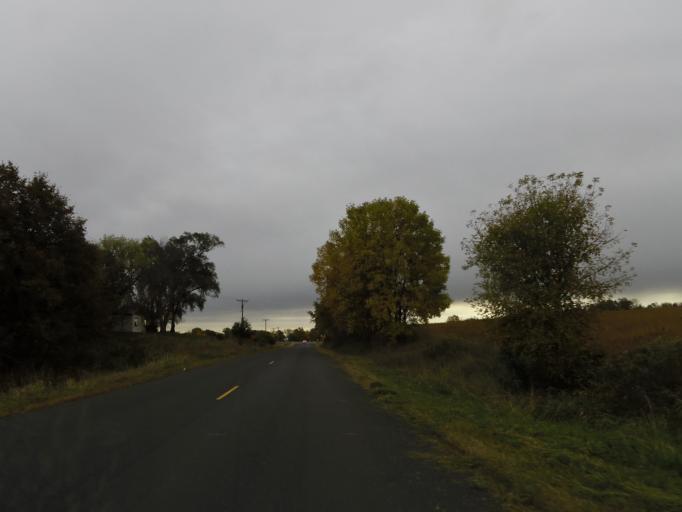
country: US
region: Minnesota
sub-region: Scott County
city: Prior Lake
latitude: 44.7036
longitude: -93.4950
